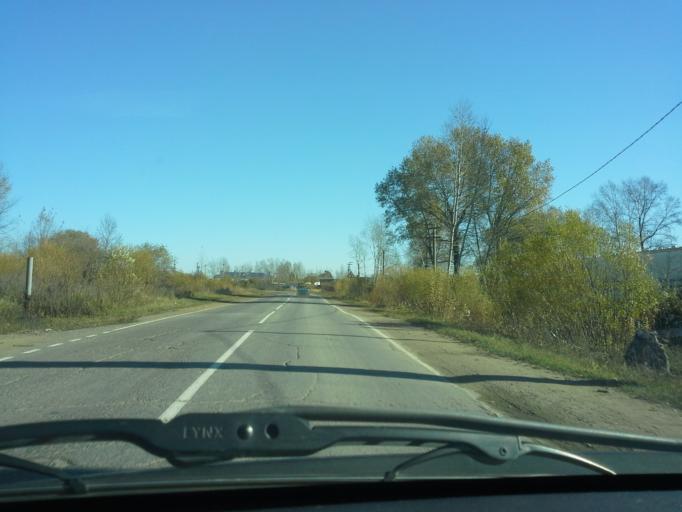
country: RU
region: Jewish Autonomous Oblast
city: Priamurskiy
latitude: 48.5361
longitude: 134.9036
